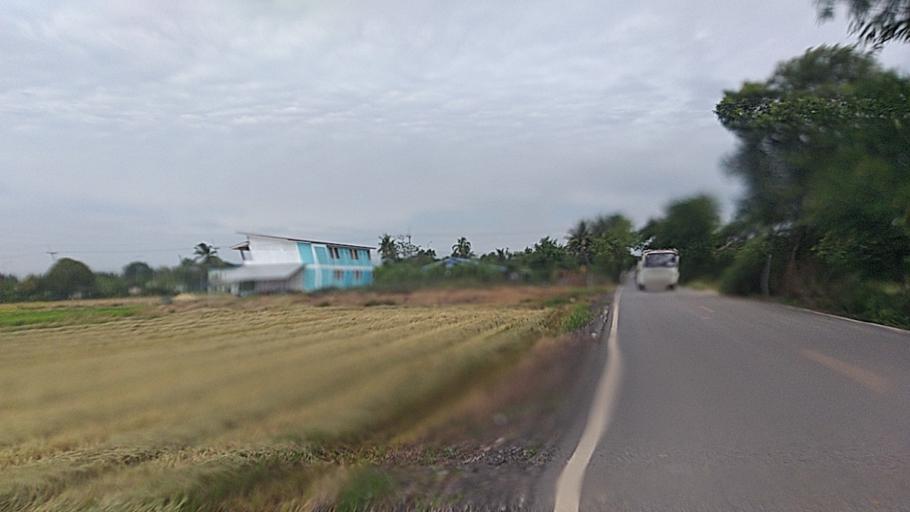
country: TH
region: Pathum Thani
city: Ban Lam Luk Ka
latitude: 14.0341
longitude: 100.8712
